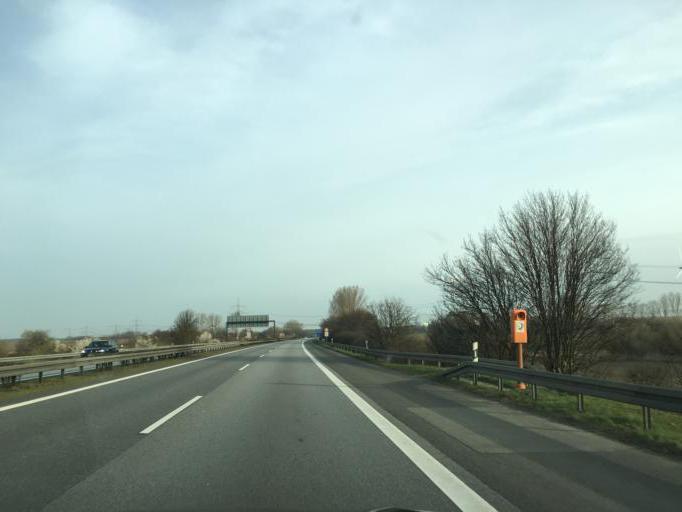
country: DE
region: Berlin
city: Blankenfelde
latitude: 52.6528
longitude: 13.4160
